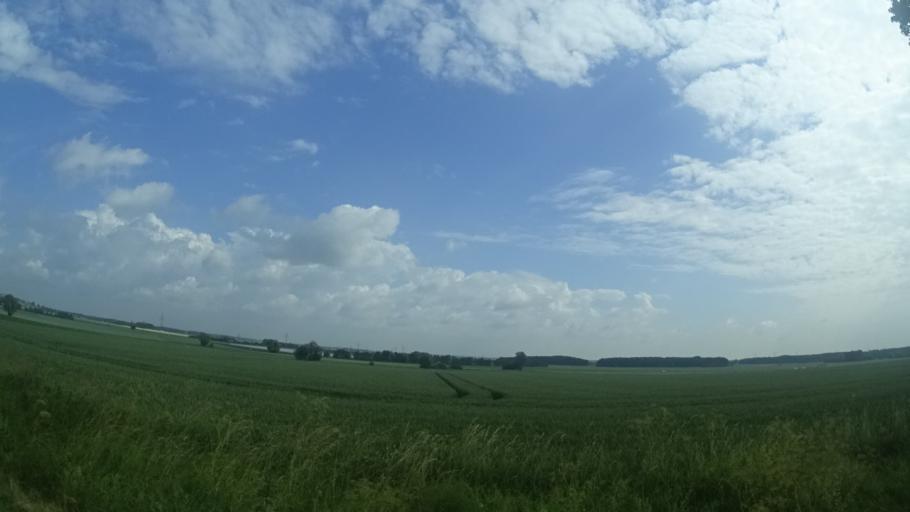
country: DE
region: Lower Saxony
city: Pattensen
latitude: 52.2194
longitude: 9.6908
